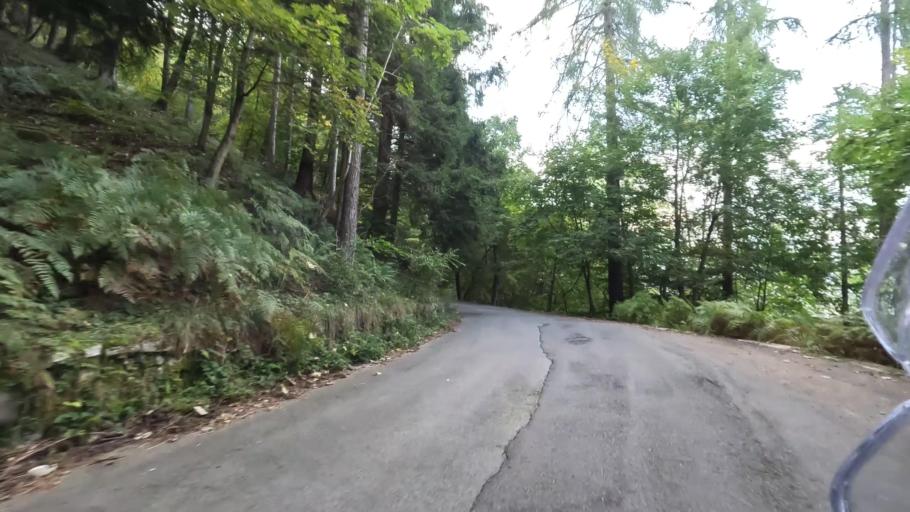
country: IT
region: Lombardy
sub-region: Provincia di Como
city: Pigra
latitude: 45.9613
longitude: 9.1258
